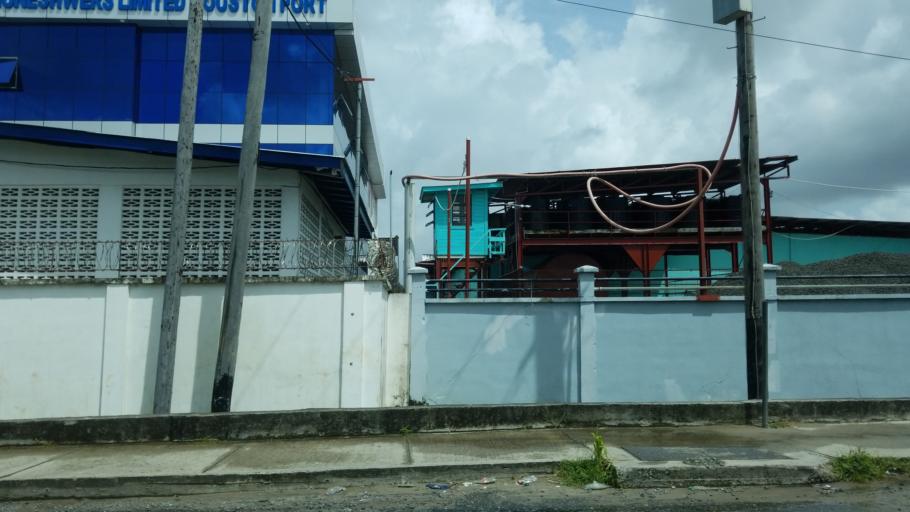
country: GY
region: Demerara-Mahaica
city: Georgetown
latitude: 6.7854
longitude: -58.1690
